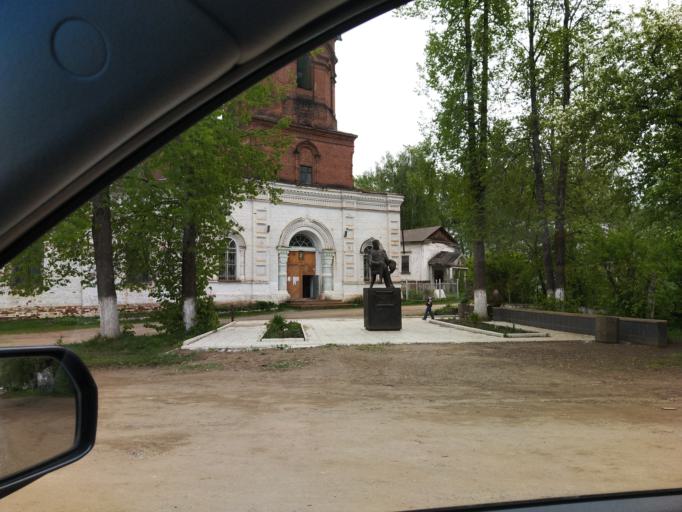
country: RU
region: Perm
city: Pavlovskiy
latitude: 57.8424
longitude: 54.8359
